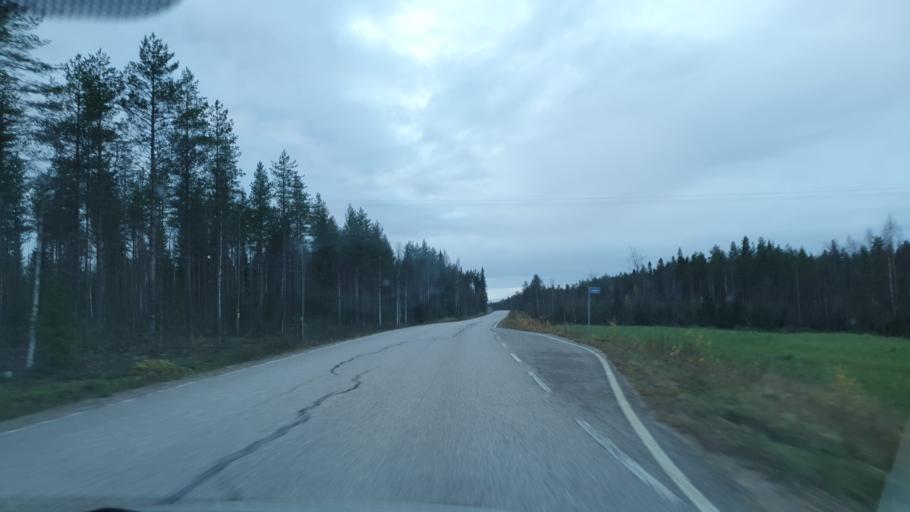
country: FI
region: Kainuu
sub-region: Kajaani
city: Ristijaervi
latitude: 64.4226
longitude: 28.4023
